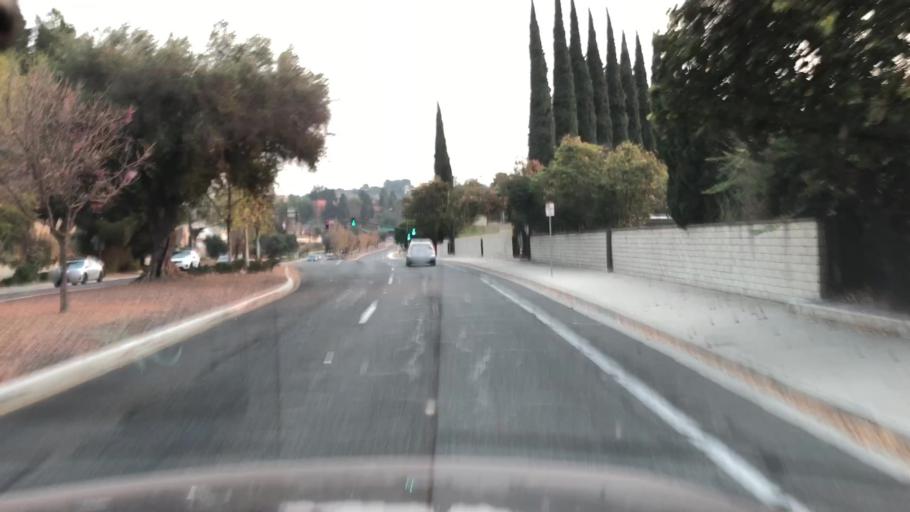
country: US
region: California
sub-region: Ventura County
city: Casa Conejo
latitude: 34.2131
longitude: -118.8875
